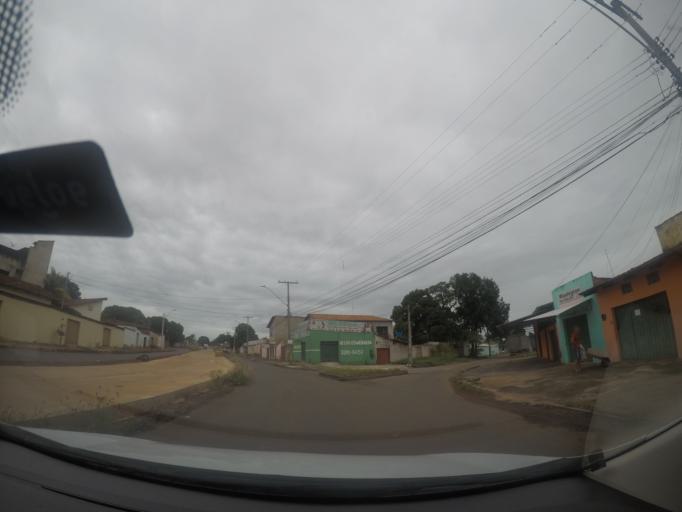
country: BR
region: Goias
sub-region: Goiania
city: Goiania
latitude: -16.6172
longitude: -49.2942
